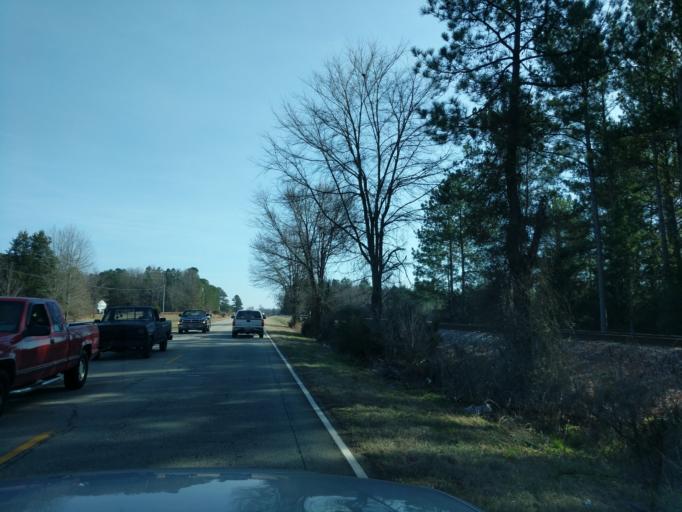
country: US
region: South Carolina
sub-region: Spartanburg County
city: Woodruff
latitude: 34.6803
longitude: -81.9846
